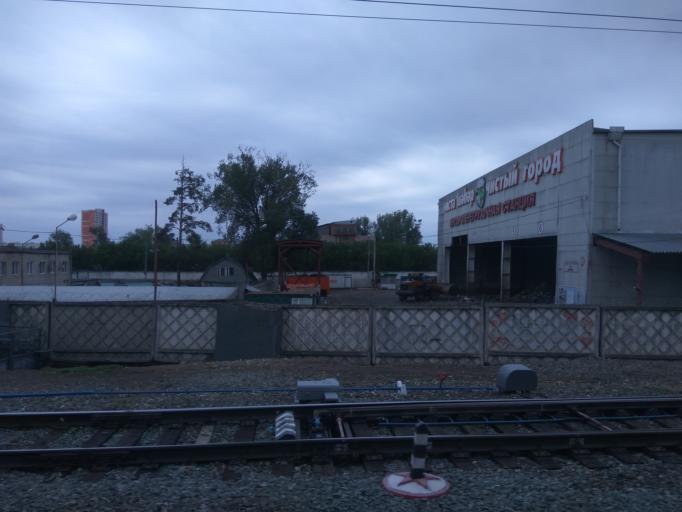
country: RU
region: Tatarstan
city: Staroye Arakchino
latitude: 55.8403
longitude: 49.0504
